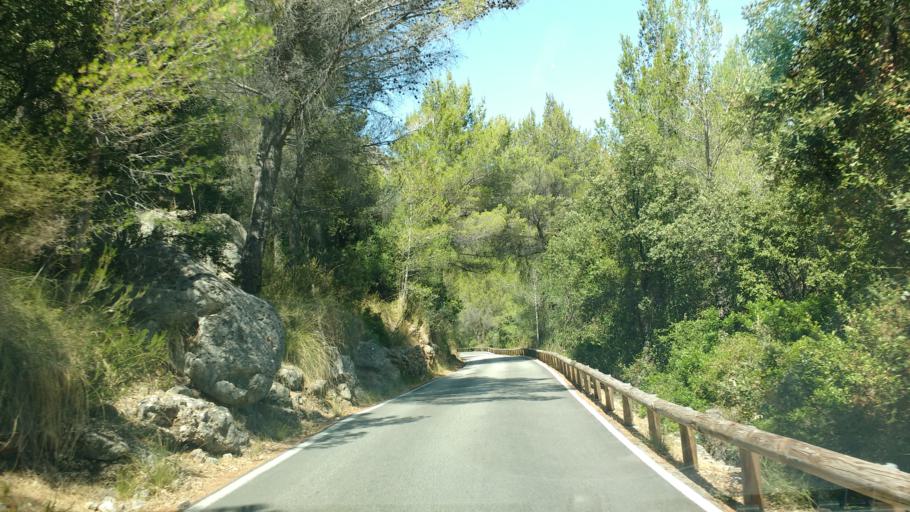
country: ES
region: Balearic Islands
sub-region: Illes Balears
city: Escorca
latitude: 39.8389
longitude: 2.7969
